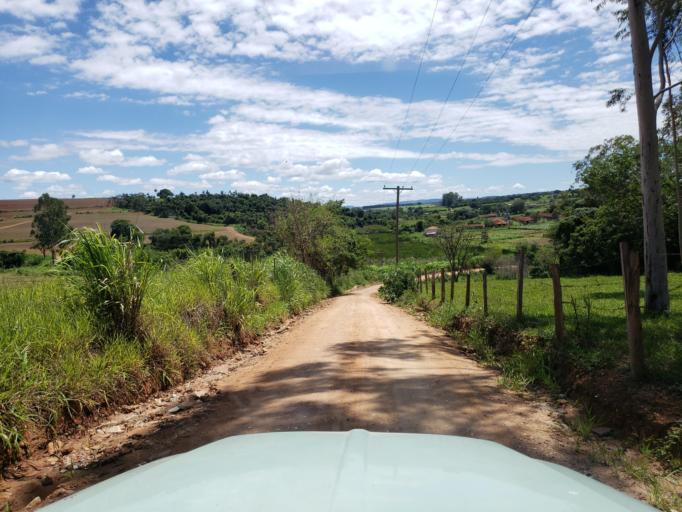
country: BR
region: Sao Paulo
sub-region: Moji-Guacu
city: Mogi-Gaucu
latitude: -22.3018
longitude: -46.9030
